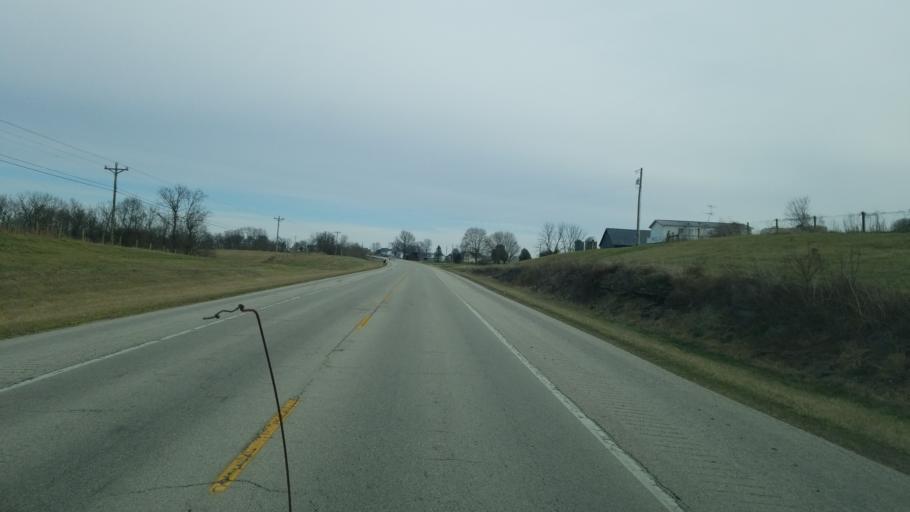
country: US
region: Kentucky
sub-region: Fleming County
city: Flemingsburg
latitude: 38.4776
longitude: -83.8848
